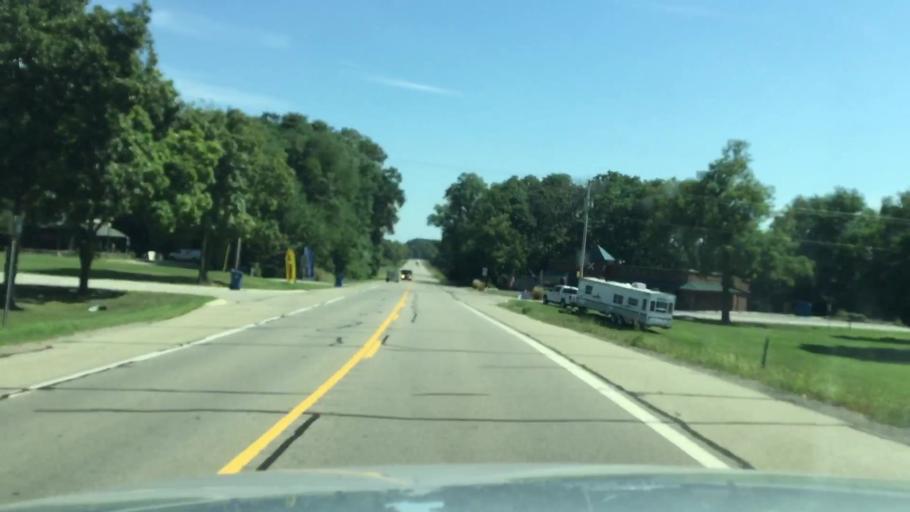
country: US
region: Michigan
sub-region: Jackson County
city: Brooklyn
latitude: 42.0599
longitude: -84.2026
